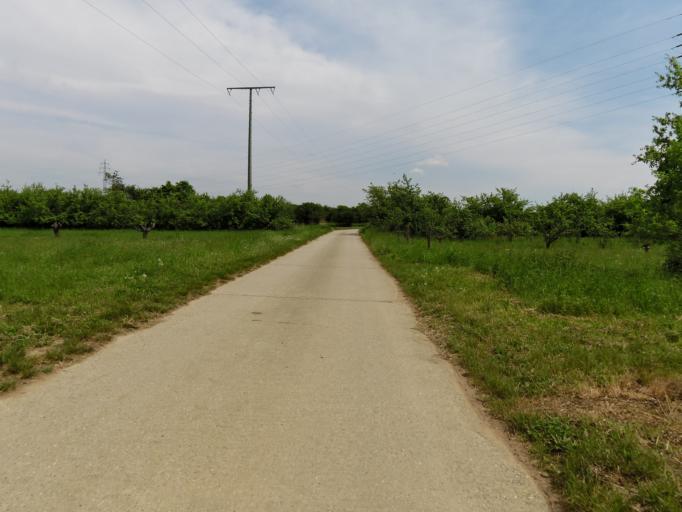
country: DE
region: Rheinland-Pfalz
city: Birkenheide
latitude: 49.4949
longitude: 8.2472
